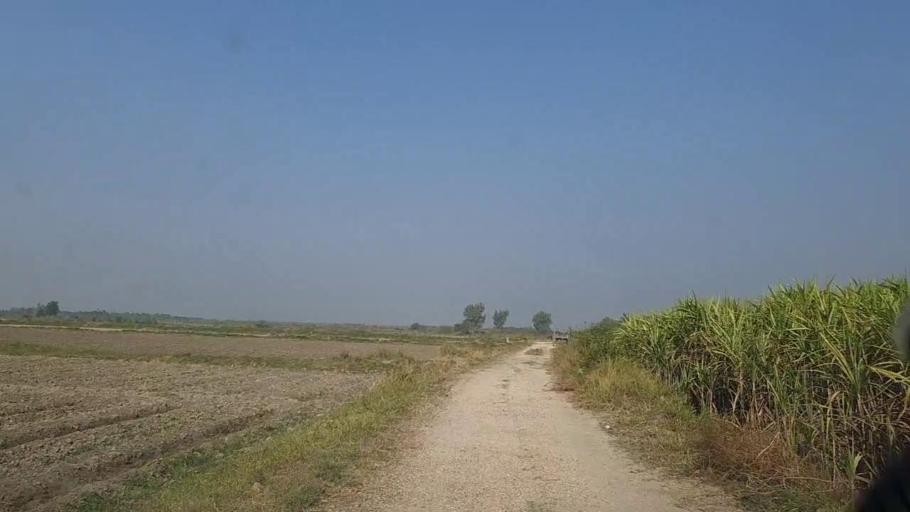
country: PK
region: Sindh
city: Thatta
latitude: 24.6556
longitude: 67.9175
